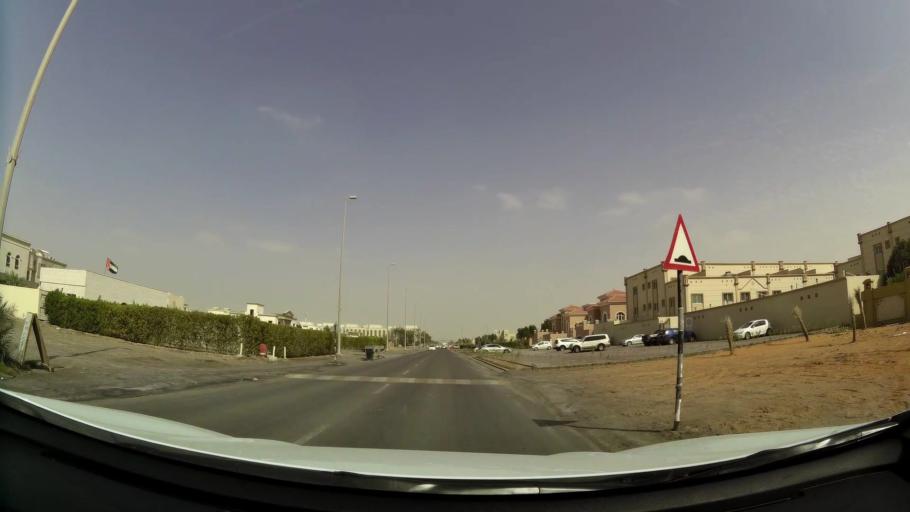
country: AE
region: Abu Dhabi
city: Abu Dhabi
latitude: 24.4177
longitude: 54.5616
